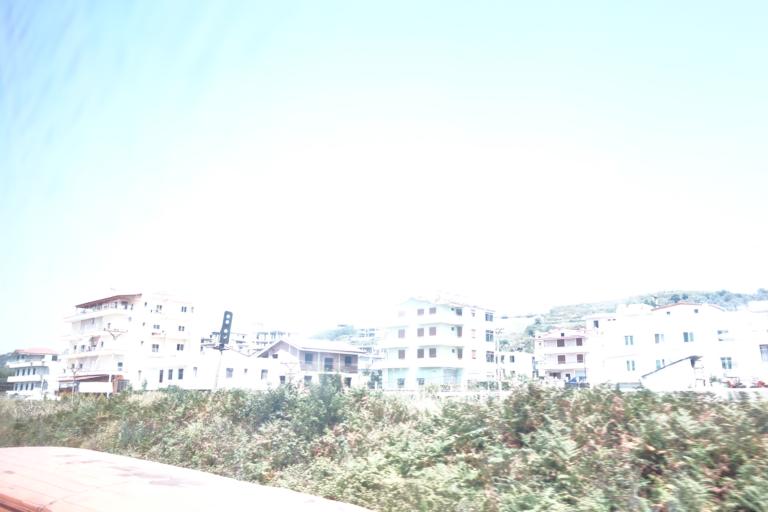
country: AL
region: Tirane
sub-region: Rrethi i Kavajes
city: Golem
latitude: 41.2511
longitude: 19.5261
